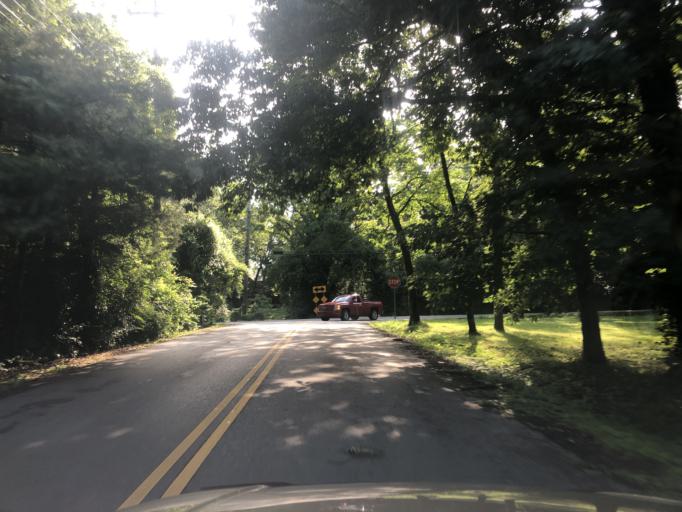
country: US
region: Tennessee
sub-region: Davidson County
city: Lakewood
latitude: 36.2321
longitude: -86.7150
